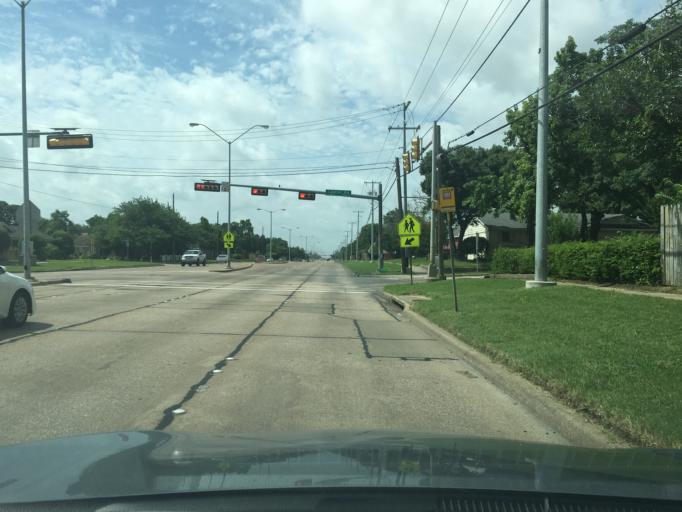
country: US
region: Texas
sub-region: Dallas County
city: Richardson
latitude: 32.9244
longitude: -96.7003
